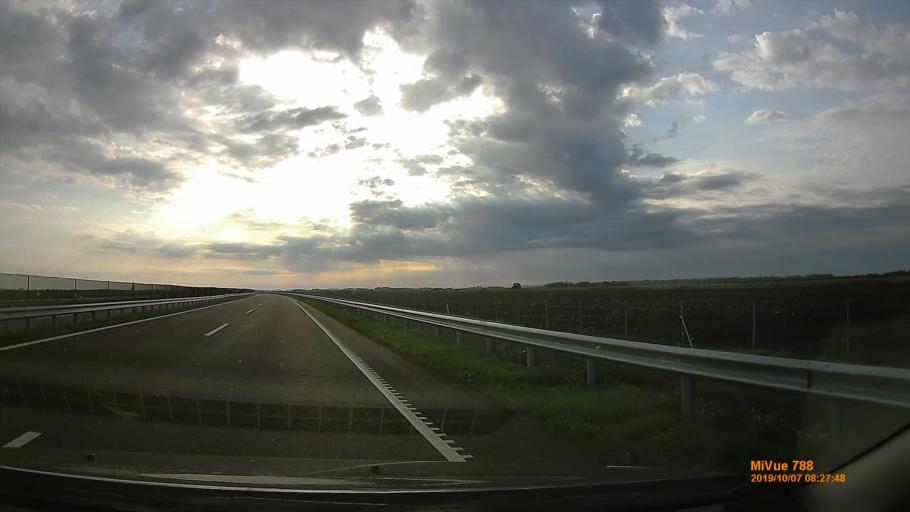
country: HU
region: Jasz-Nagykun-Szolnok
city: Ocsod
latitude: 46.8137
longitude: 20.3884
